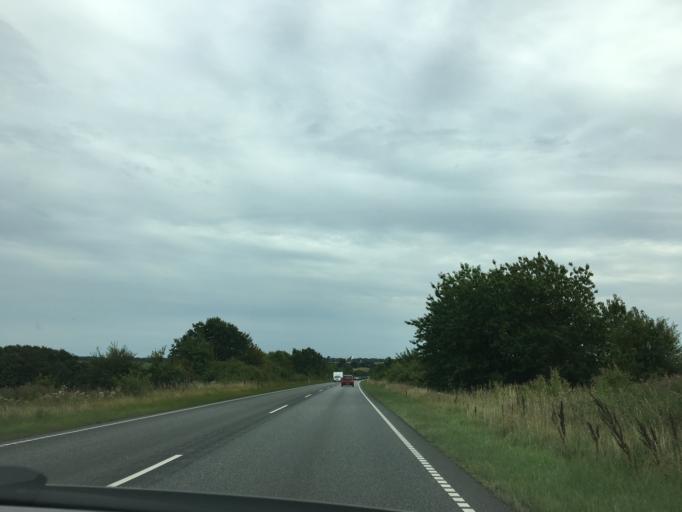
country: DK
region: South Denmark
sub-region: Vejle Kommune
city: Borkop
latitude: 55.6567
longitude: 9.6310
